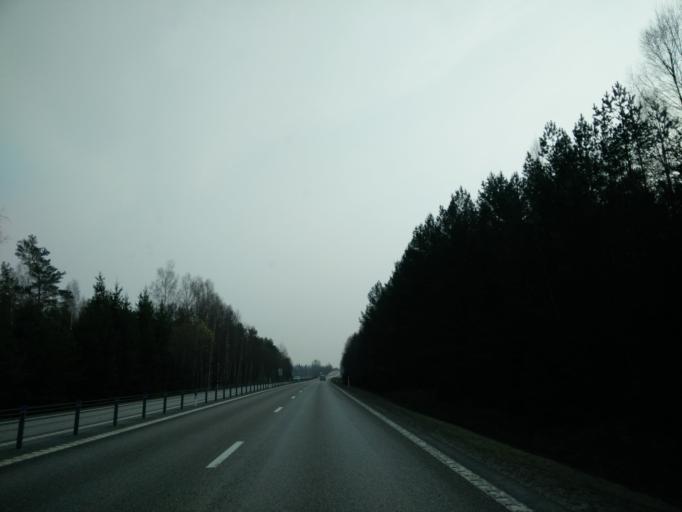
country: SE
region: Vaermland
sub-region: Forshaga Kommun
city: Forshaga
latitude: 59.4509
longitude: 13.4168
